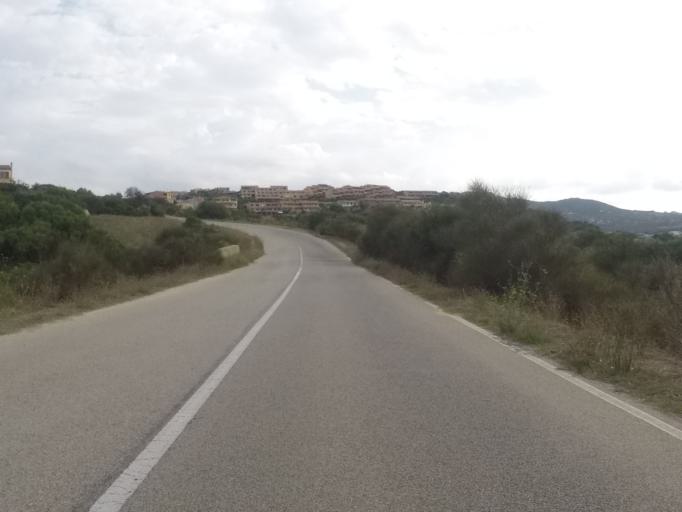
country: IT
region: Sardinia
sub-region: Provincia di Olbia-Tempio
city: Palau
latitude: 41.1820
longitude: 9.3762
